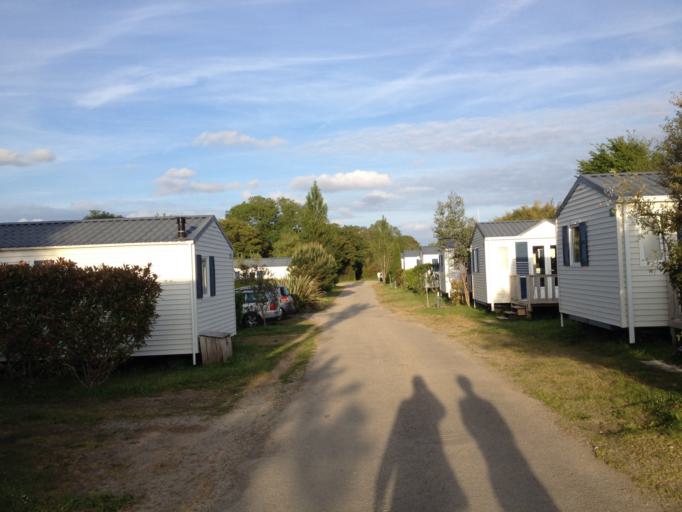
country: FR
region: Brittany
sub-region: Departement du Finistere
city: Roscanvel
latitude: 48.3649
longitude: -4.5379
